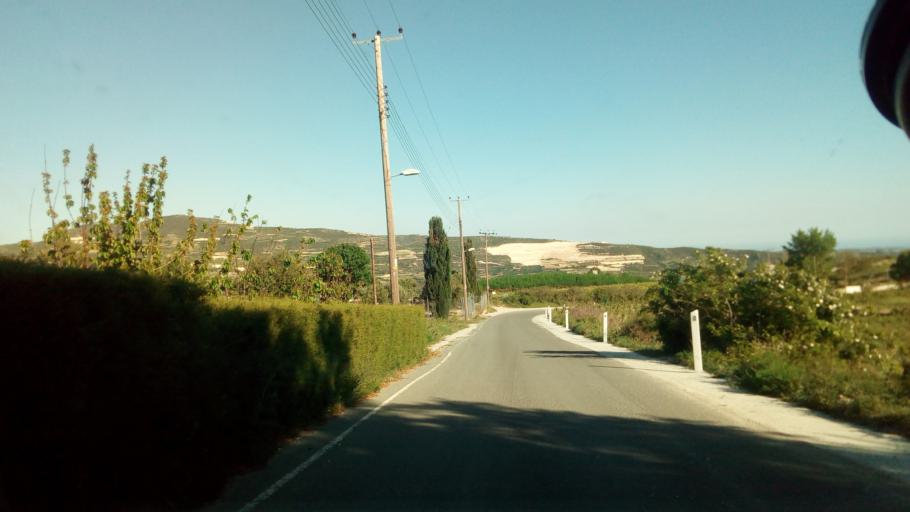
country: CY
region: Limassol
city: Pachna
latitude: 34.8606
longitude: 32.8036
